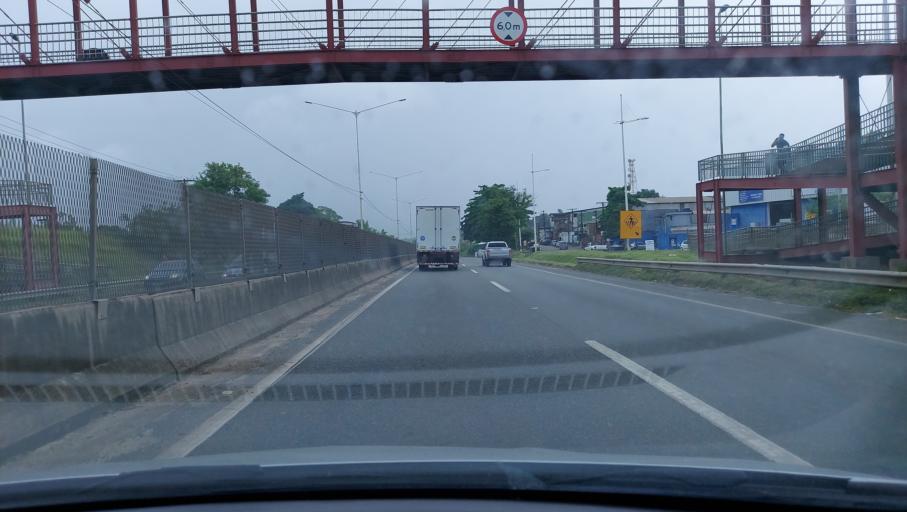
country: BR
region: Bahia
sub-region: Salvador
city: Salvador
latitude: -12.8876
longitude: -38.4404
